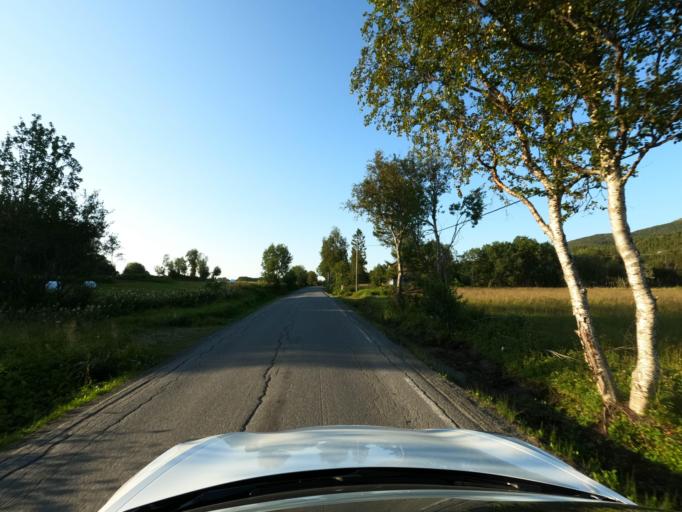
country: NO
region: Troms
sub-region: Skanland
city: Evenskjer
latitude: 68.4685
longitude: 16.7022
